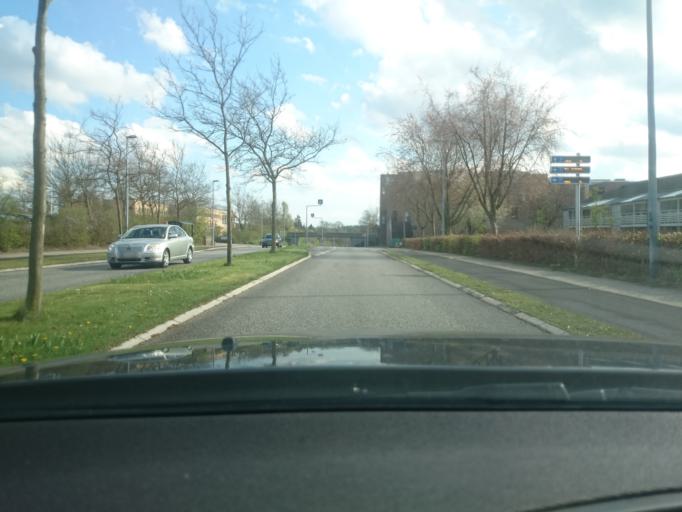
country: DK
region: Capital Region
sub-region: Fureso Kommune
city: Vaerlose
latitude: 55.7847
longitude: 12.3764
